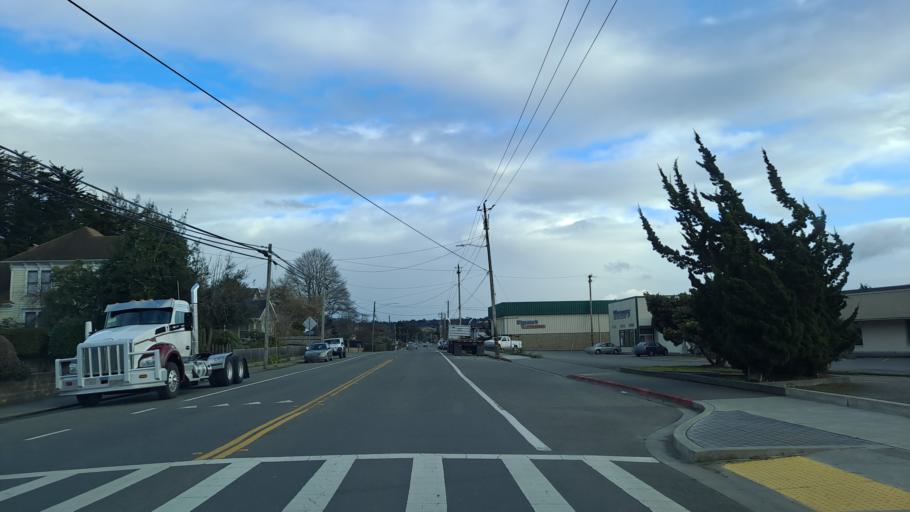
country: US
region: California
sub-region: Humboldt County
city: Fortuna
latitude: 40.5964
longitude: -124.1456
